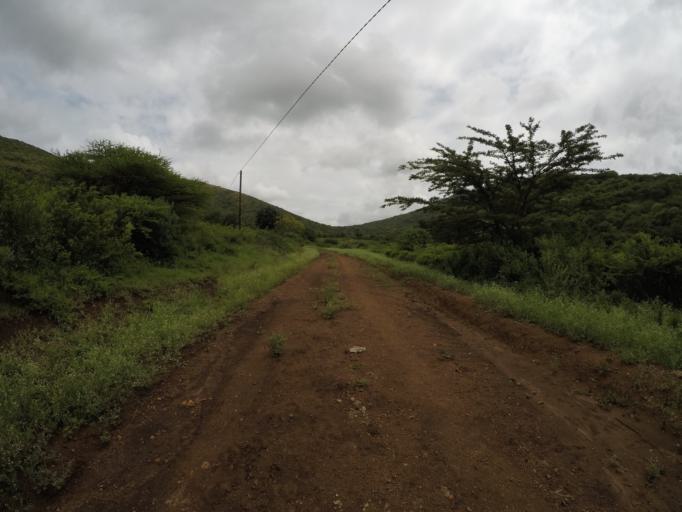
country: ZA
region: KwaZulu-Natal
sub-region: uThungulu District Municipality
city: Empangeni
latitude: -28.5831
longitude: 31.8872
